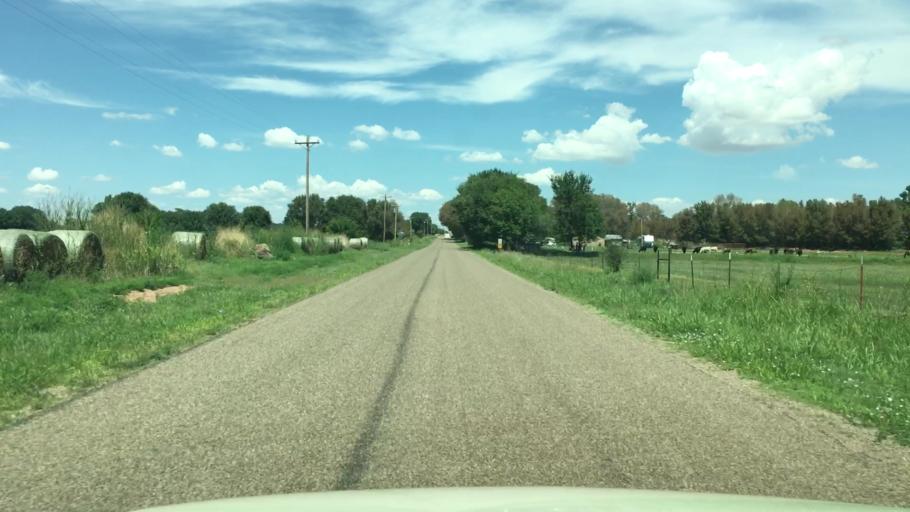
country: US
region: New Mexico
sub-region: De Baca County
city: Fort Sumner
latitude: 34.4351
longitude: -104.1936
